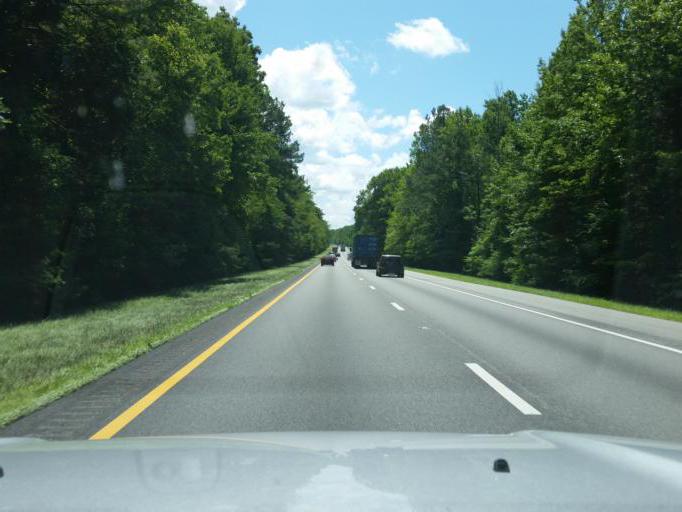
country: US
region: Virginia
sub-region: King William County
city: West Point
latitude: 37.4343
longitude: -76.8469
